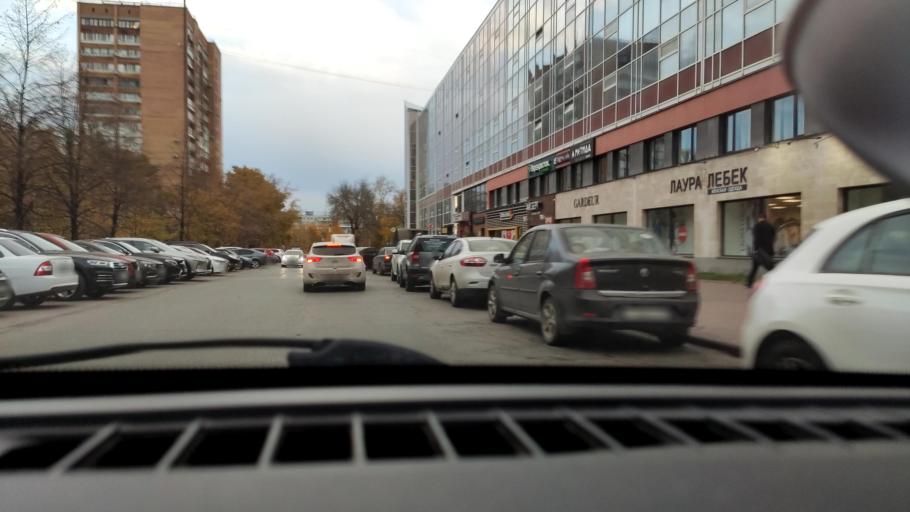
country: RU
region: Samara
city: Samara
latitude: 53.2014
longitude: 50.1410
